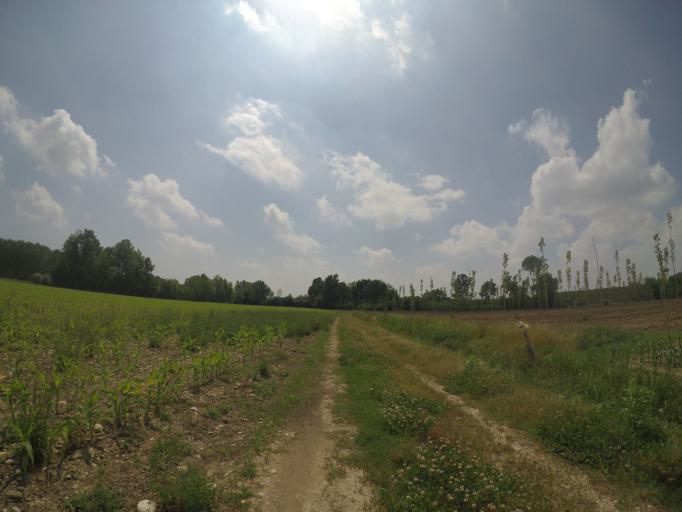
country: IT
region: Friuli Venezia Giulia
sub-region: Provincia di Udine
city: Bertiolo
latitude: 45.9319
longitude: 13.0318
